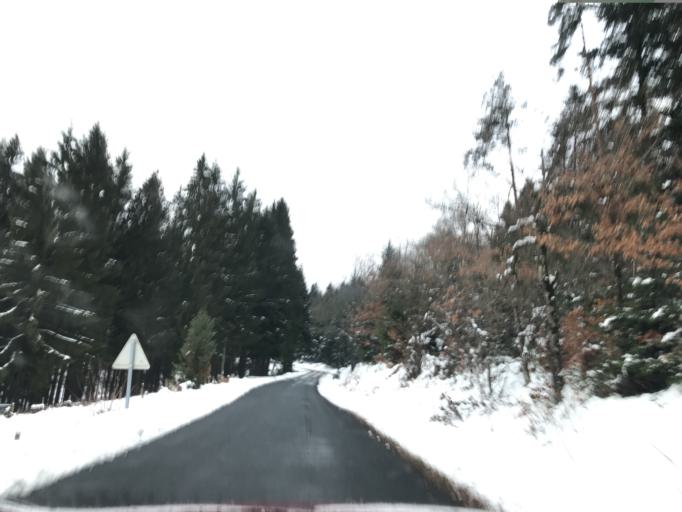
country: FR
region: Auvergne
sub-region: Departement du Puy-de-Dome
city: Celles-sur-Durolle
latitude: 45.7515
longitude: 3.6645
